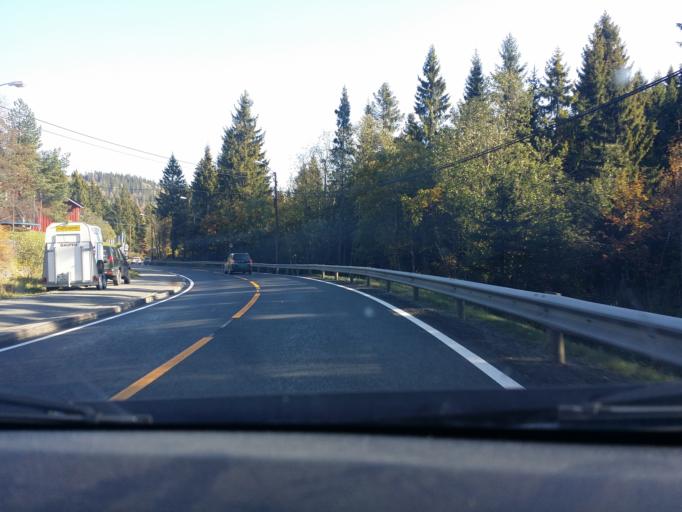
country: NO
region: Akershus
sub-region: Baerum
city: Skui
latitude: 59.9587
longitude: 10.3622
